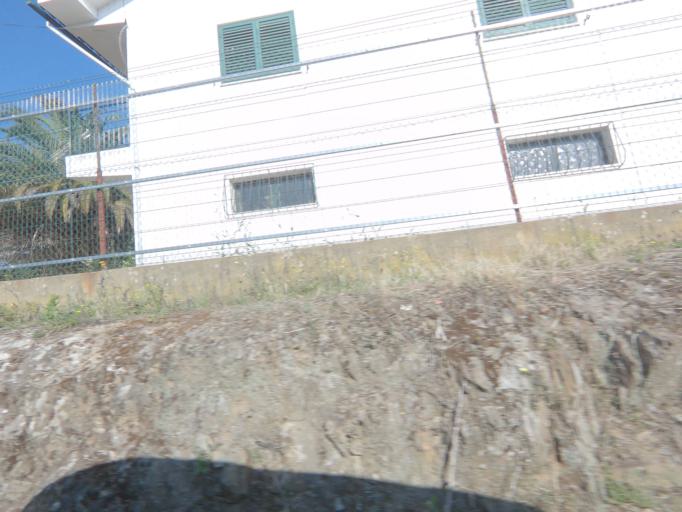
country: PT
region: Vila Real
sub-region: Sabrosa
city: Sabrosa
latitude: 41.2551
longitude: -7.5976
